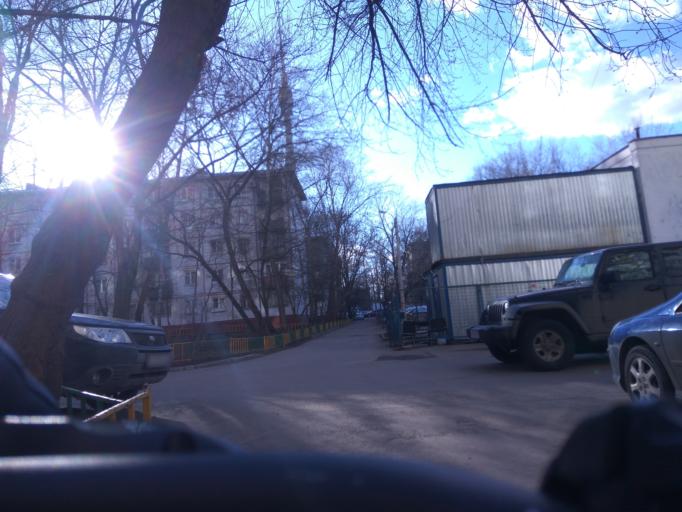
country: RU
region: Moscow
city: Ostankinskiy
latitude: 55.8203
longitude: 37.6246
